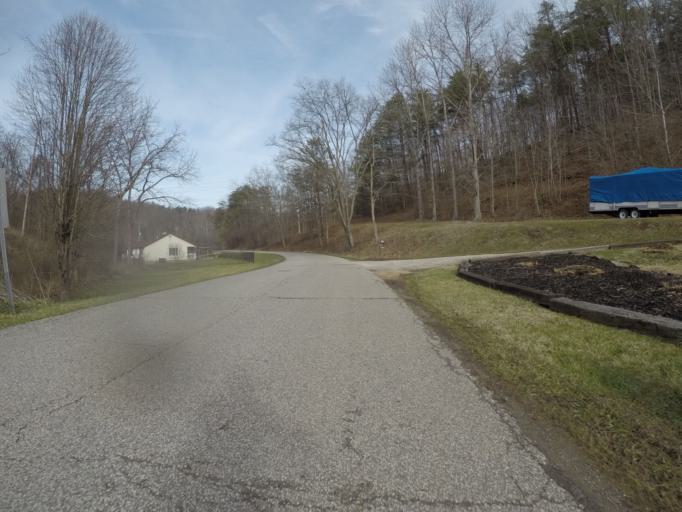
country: US
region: West Virginia
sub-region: Wayne County
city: Lavalette
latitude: 38.3507
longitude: -82.3732
